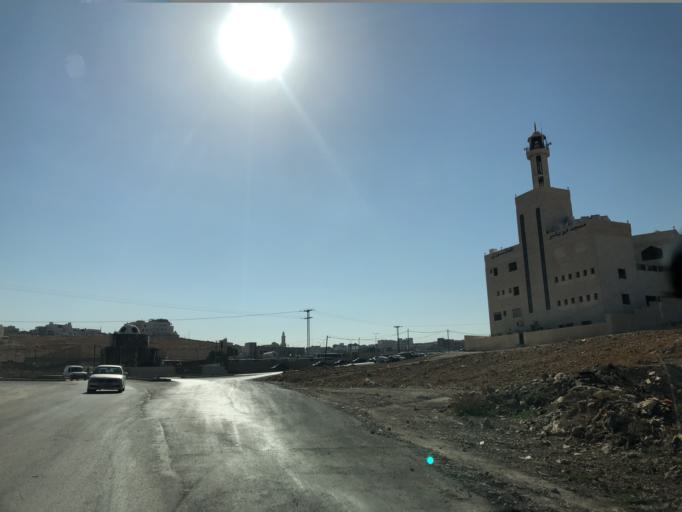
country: JO
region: Amman
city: Wadi as Sir
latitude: 31.9343
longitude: 35.8441
